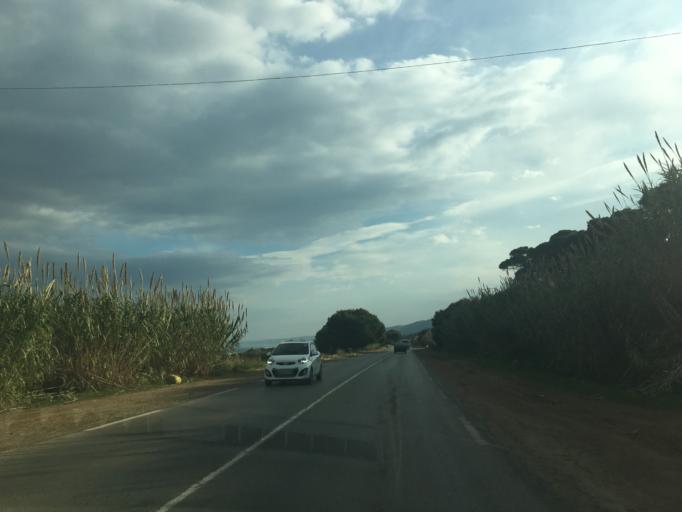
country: DZ
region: Tipaza
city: Tipasa
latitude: 36.5896
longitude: 2.4997
